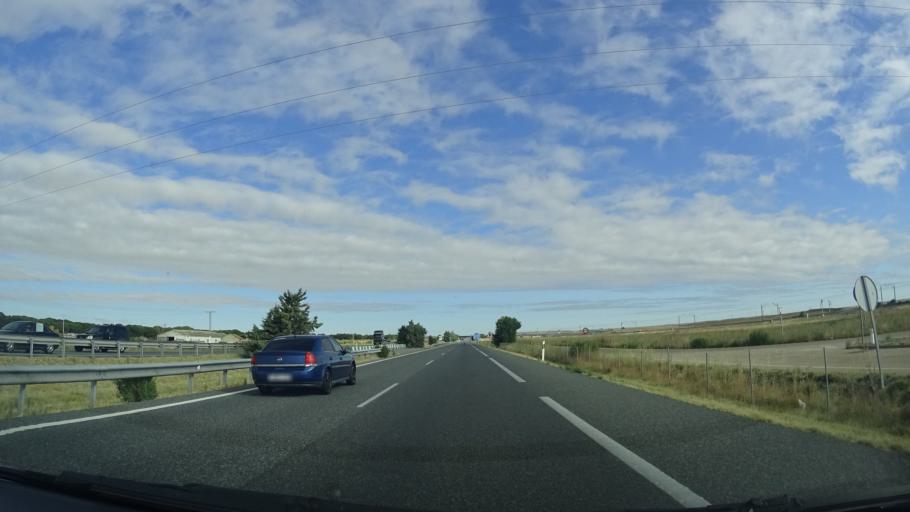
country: ES
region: Castille and Leon
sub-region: Provincia de Valladolid
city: Medina del Campo
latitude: 41.2757
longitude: -4.8888
